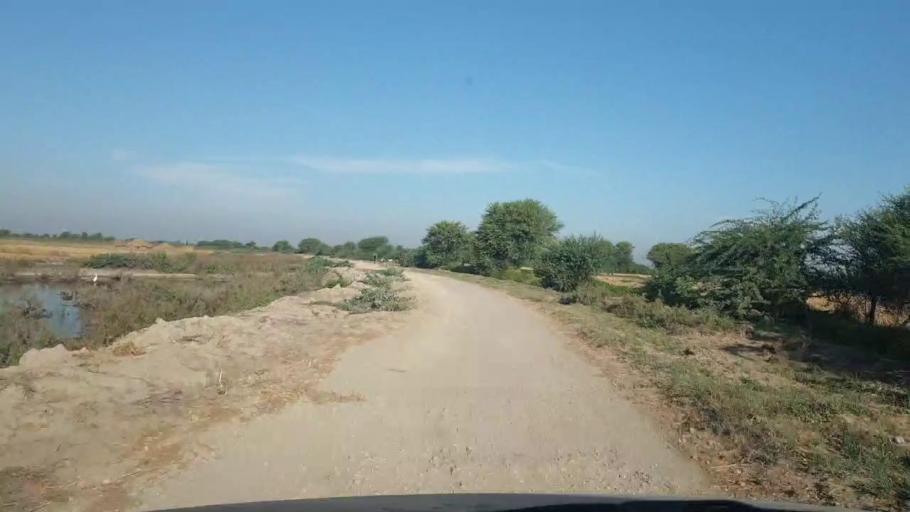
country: PK
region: Sindh
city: Talhar
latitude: 24.8237
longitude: 68.8234
